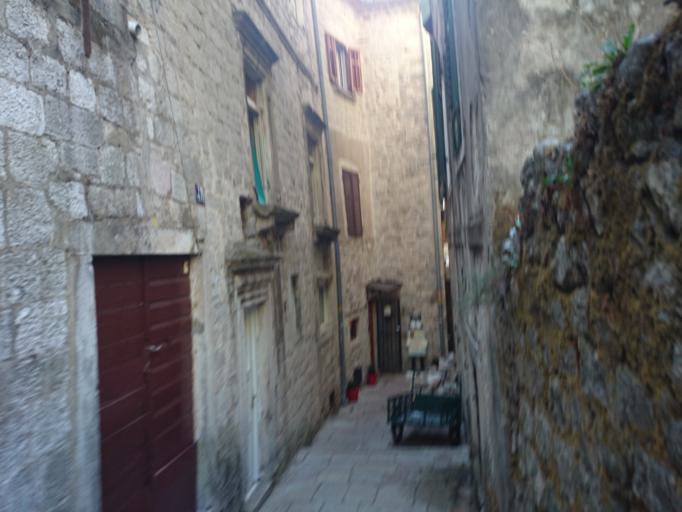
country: ME
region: Kotor
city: Kotor
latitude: 42.4254
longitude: 18.7722
